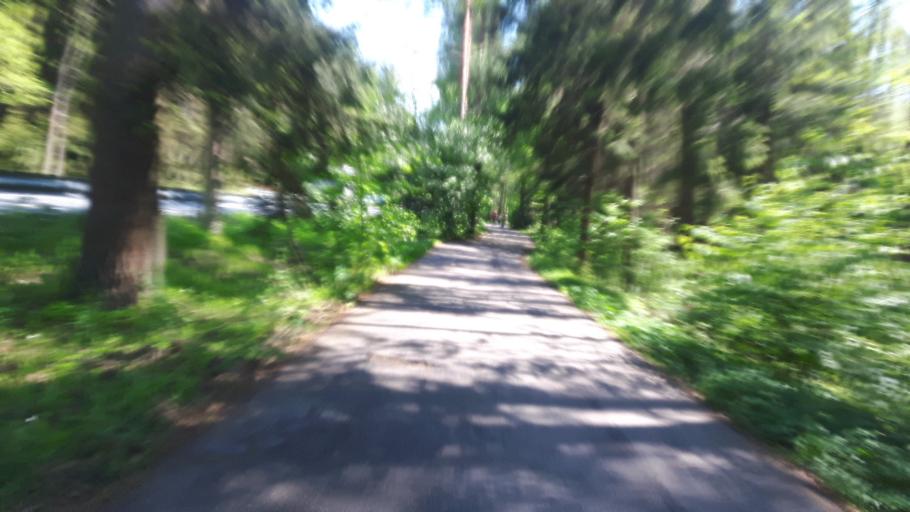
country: RU
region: St.-Petersburg
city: Komarovo
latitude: 60.1779
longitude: 29.7864
